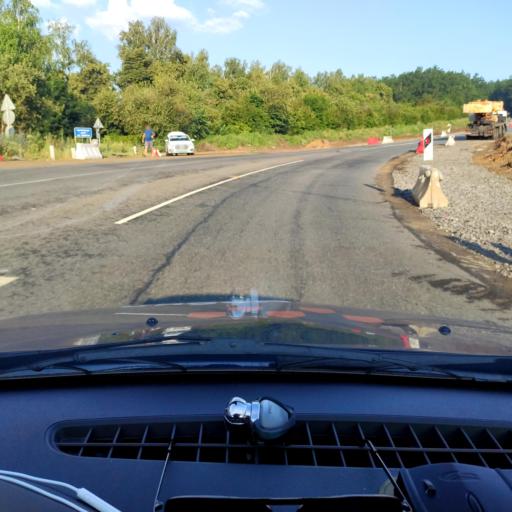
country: RU
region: Lipetsk
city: Kazaki
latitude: 52.5137
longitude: 38.1100
